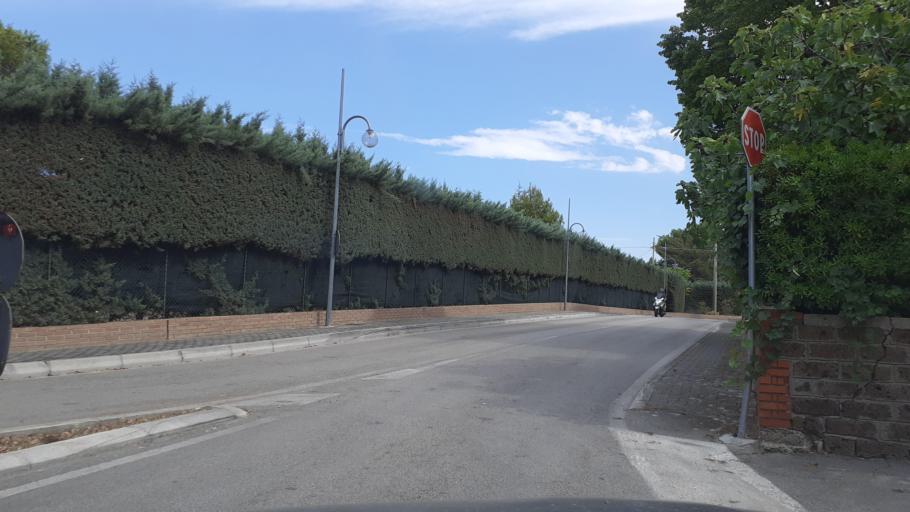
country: IT
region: Abruzzo
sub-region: Provincia di Chieti
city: Fossacesia
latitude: 42.2536
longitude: 14.4967
